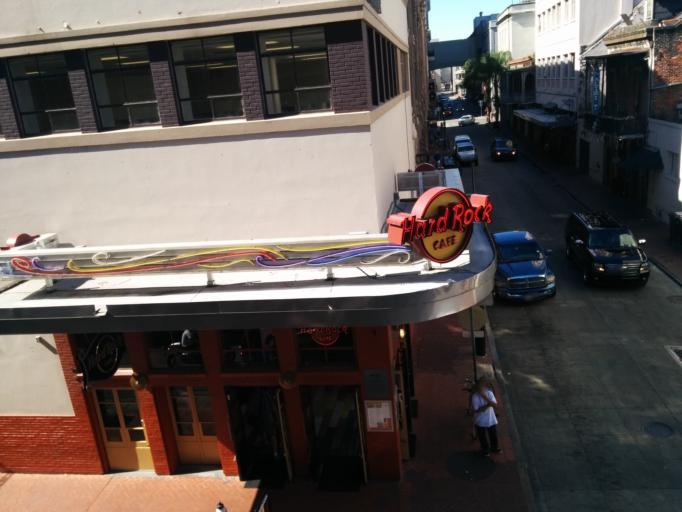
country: US
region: Louisiana
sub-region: Orleans Parish
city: New Orleans
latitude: 29.9546
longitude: -90.0691
